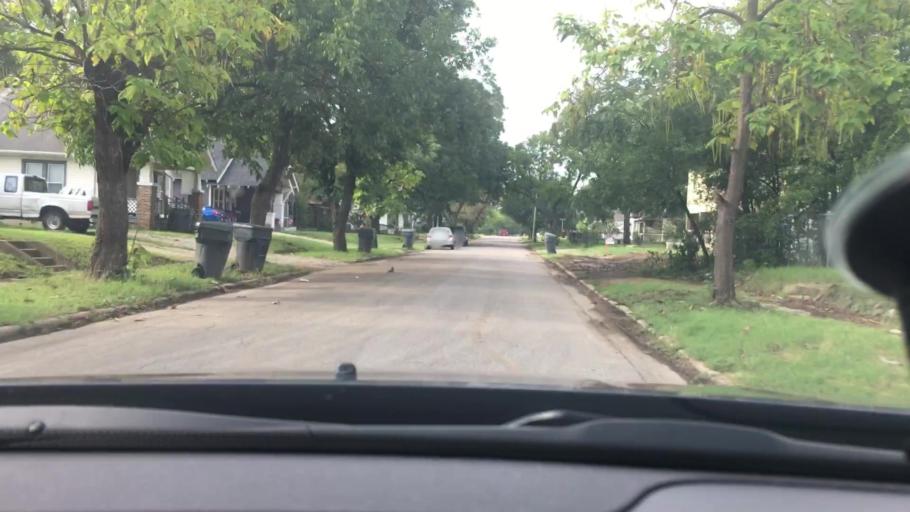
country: US
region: Oklahoma
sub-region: Carter County
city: Ardmore
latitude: 34.1797
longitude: -97.1289
